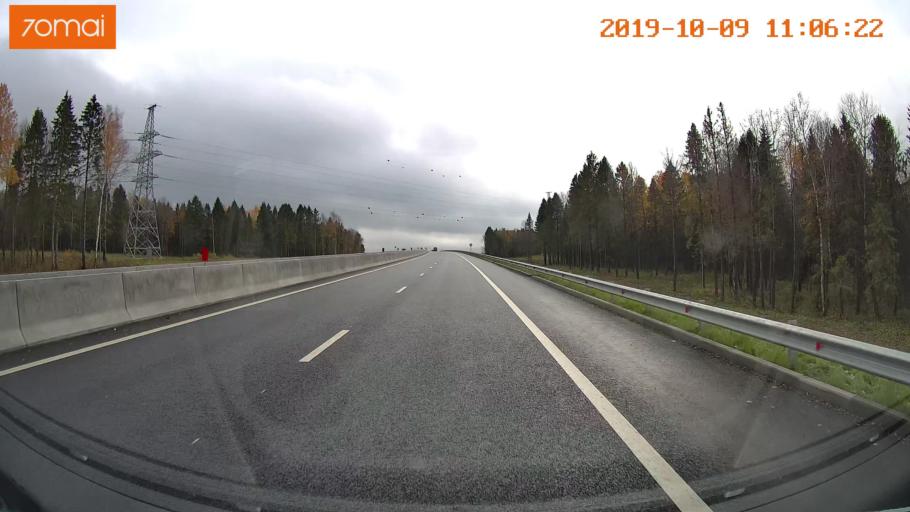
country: RU
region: Vologda
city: Vologda
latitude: 59.1874
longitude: 39.7600
